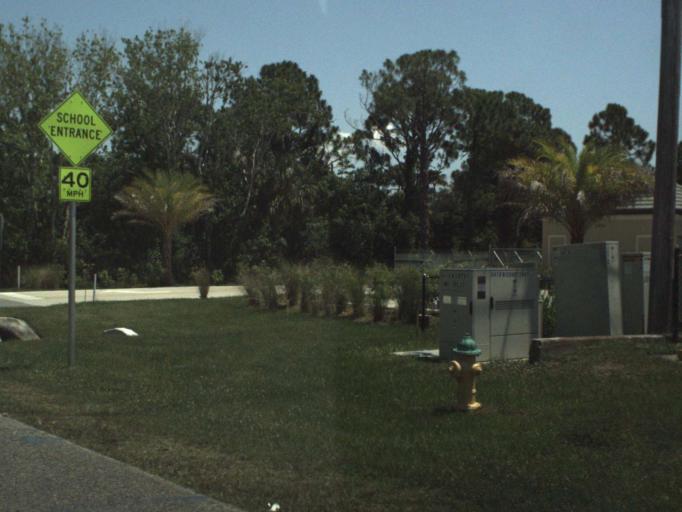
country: US
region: Florida
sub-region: Brevard County
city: Cocoa
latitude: 28.4194
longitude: -80.7068
